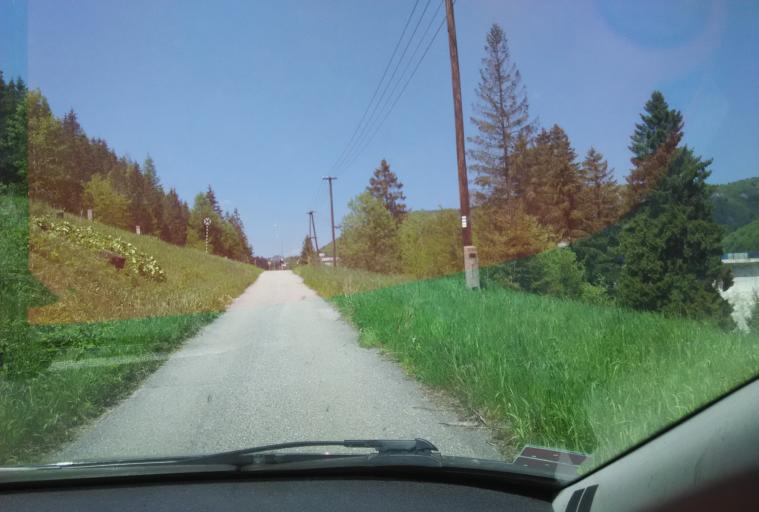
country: SK
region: Kosicky
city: Dobsina
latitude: 48.8540
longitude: 20.3837
